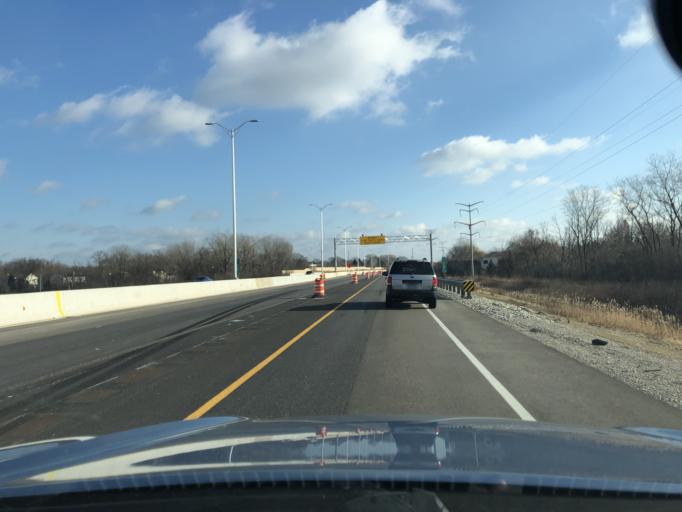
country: US
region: Illinois
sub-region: Cook County
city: Northbrook
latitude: 42.1451
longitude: -87.8168
